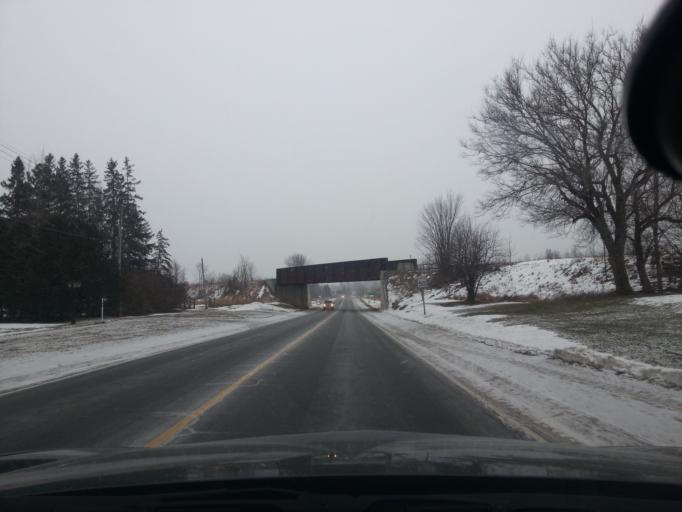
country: CA
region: Ontario
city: Arnprior
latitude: 45.3295
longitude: -76.2911
